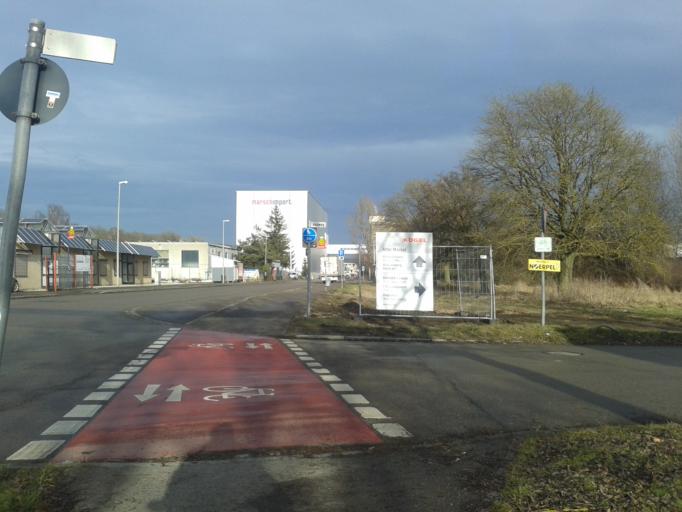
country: DE
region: Baden-Wuerttemberg
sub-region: Tuebingen Region
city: Ulm
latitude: 48.3661
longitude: 9.9422
